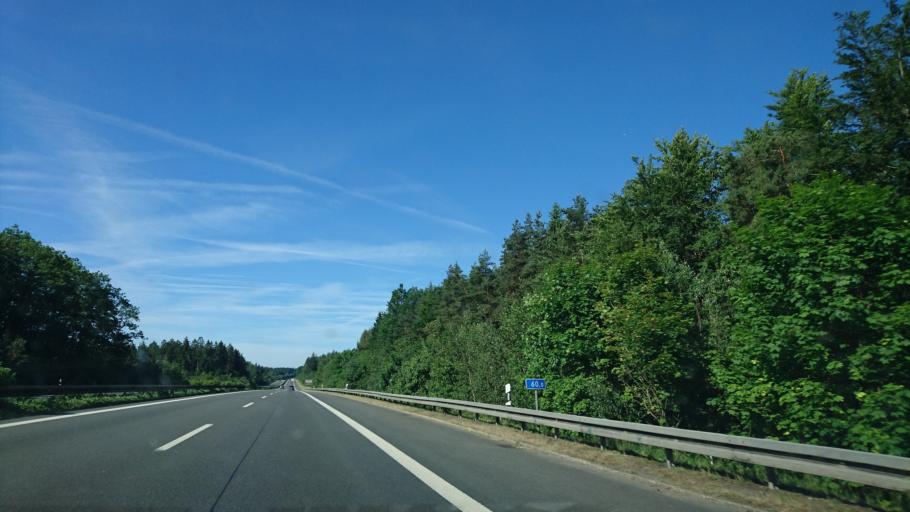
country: DE
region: Saxony
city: Waldkirchen
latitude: 50.6241
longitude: 12.4172
